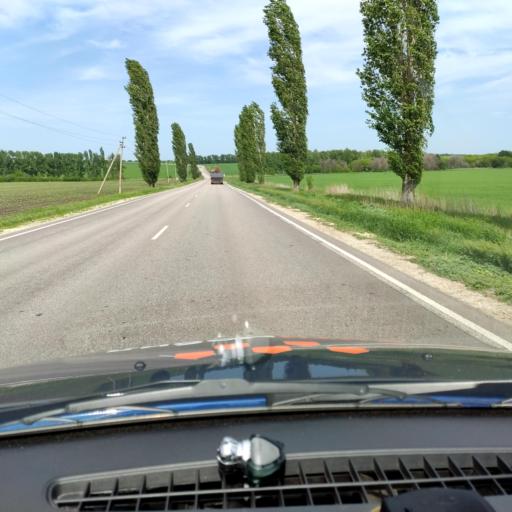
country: RU
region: Voronezj
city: Novaya Usman'
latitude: 51.5495
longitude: 39.3666
